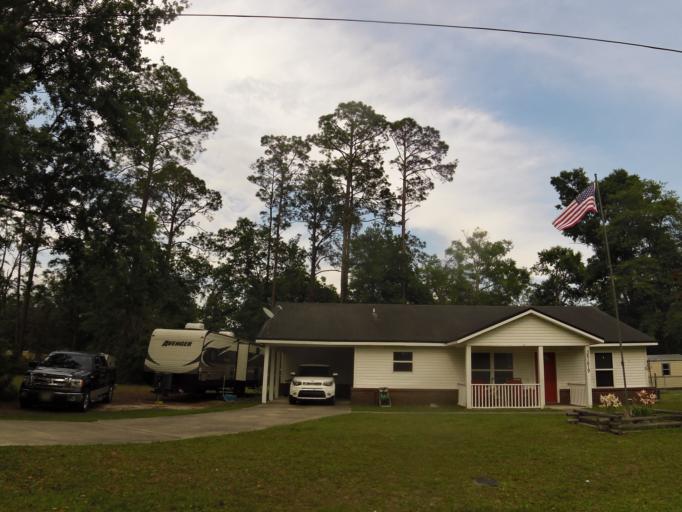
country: US
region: Florida
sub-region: Nassau County
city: Hilliard
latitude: 30.6900
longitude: -81.9237
